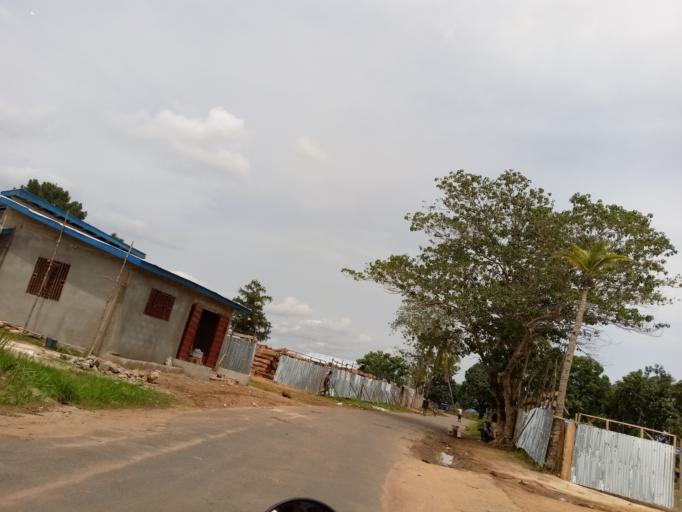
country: SL
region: Western Area
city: Waterloo
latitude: 8.3307
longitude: -13.0100
